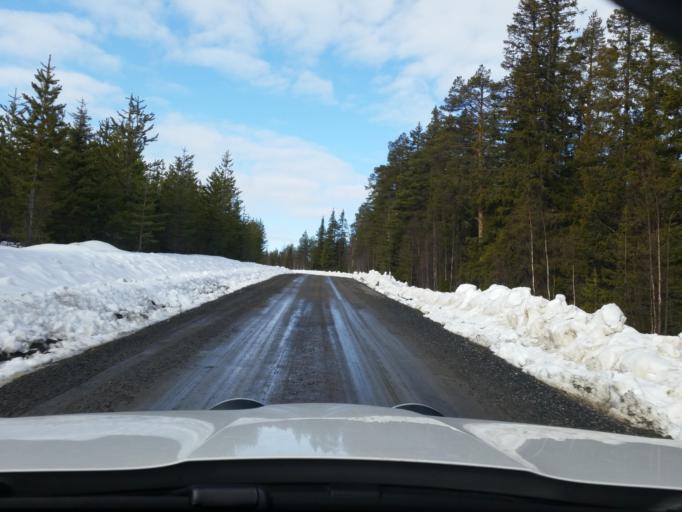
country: SE
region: Vaesterbotten
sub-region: Skelleftea Kommun
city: Storvik
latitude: 65.5104
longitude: 20.4323
